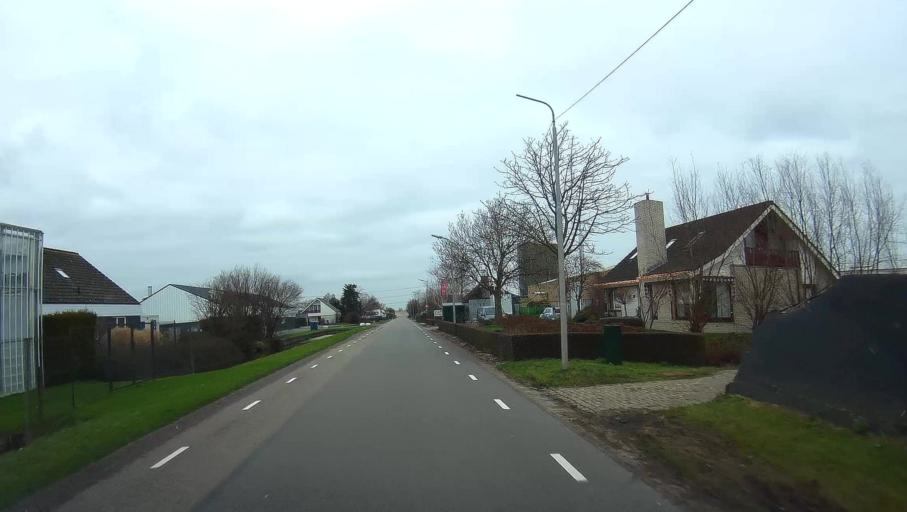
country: NL
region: South Holland
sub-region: Gemeente Lansingerland
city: Bergschenhoek
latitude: 52.0230
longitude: 4.5001
